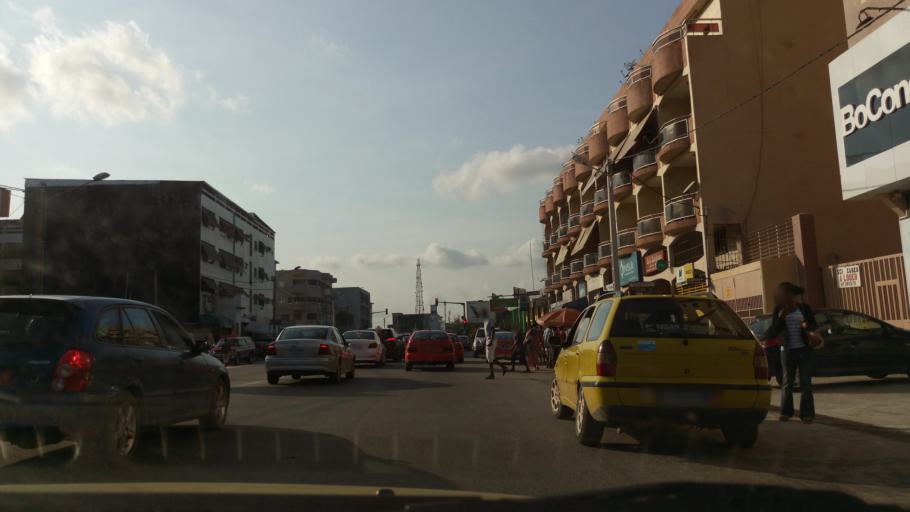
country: CI
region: Lagunes
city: Abobo
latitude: 5.3973
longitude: -3.9774
